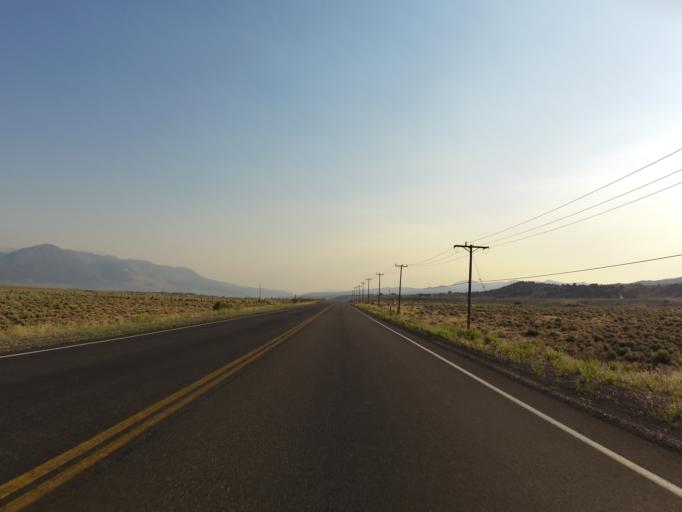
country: US
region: California
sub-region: Mono County
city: Bridgeport
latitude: 38.2267
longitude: -119.2269
